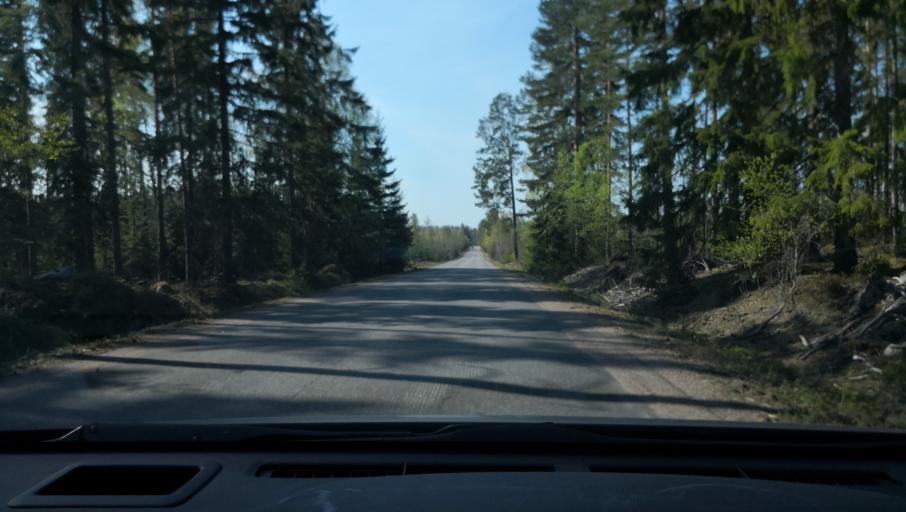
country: SE
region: Uppsala
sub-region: Heby Kommun
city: Tarnsjo
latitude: 60.2607
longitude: 16.9386
